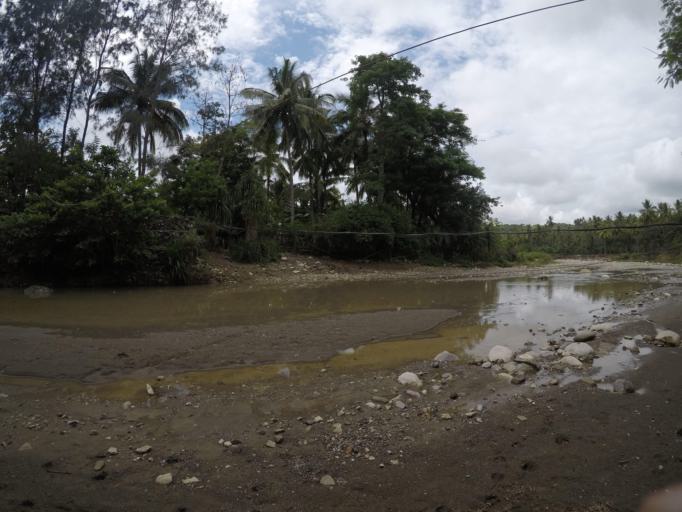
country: TL
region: Viqueque
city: Viqueque
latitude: -8.8589
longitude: 126.3623
